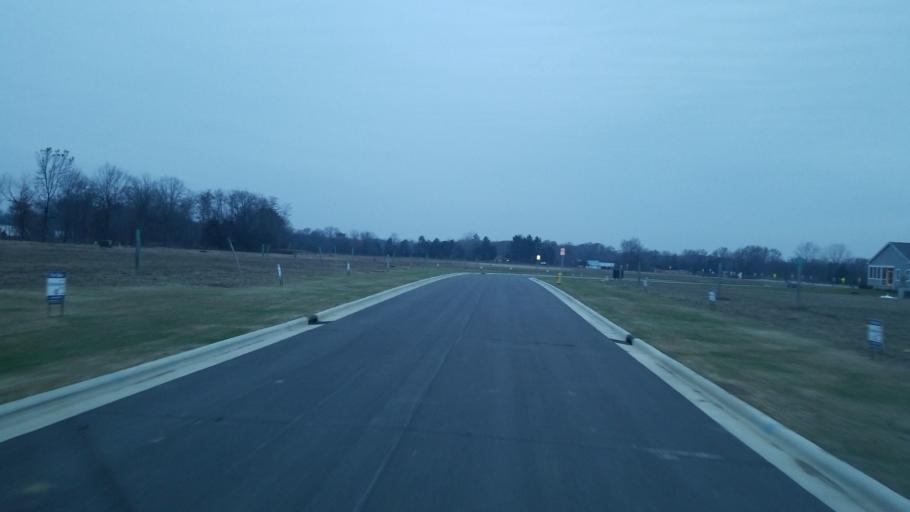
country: US
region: Ohio
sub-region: Delaware County
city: Sunbury
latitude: 40.2720
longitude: -82.9328
